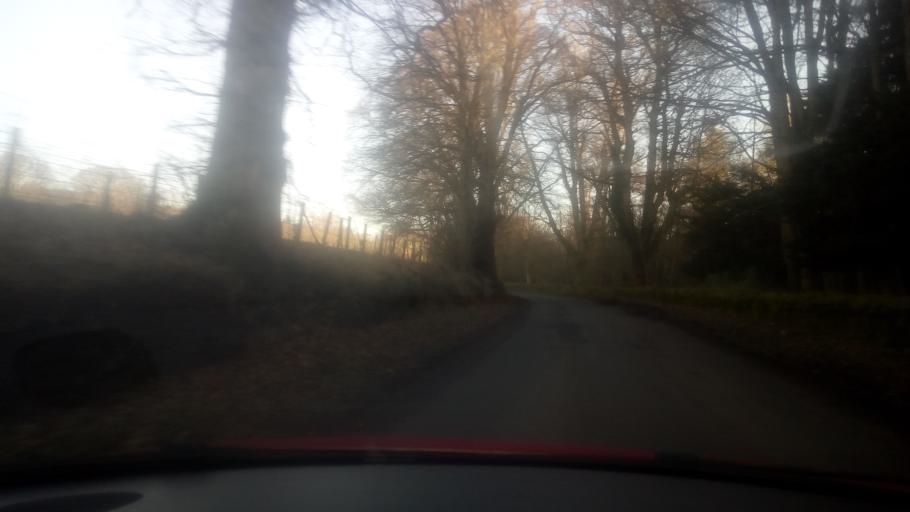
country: GB
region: Scotland
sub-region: The Scottish Borders
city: Jedburgh
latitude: 55.5168
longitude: -2.5638
